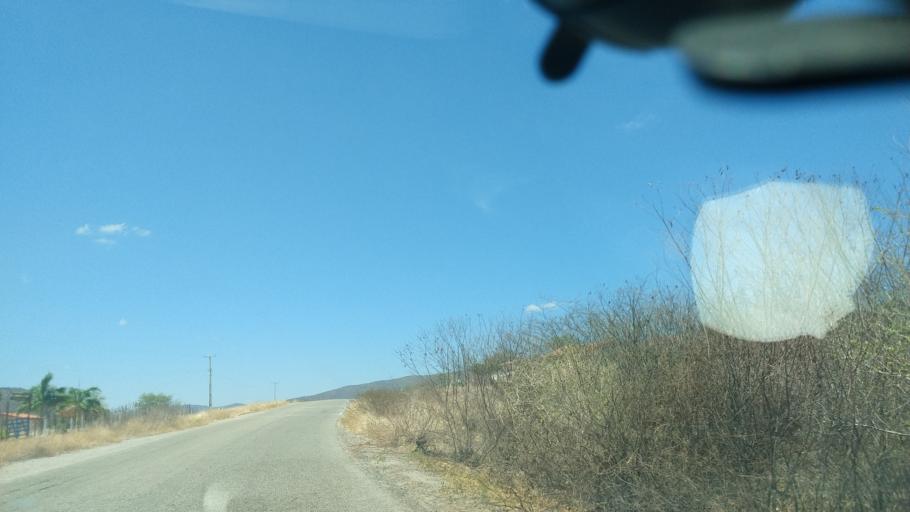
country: BR
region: Rio Grande do Norte
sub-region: Sao Tome
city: Sao Tome
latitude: -5.9775
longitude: -36.1458
